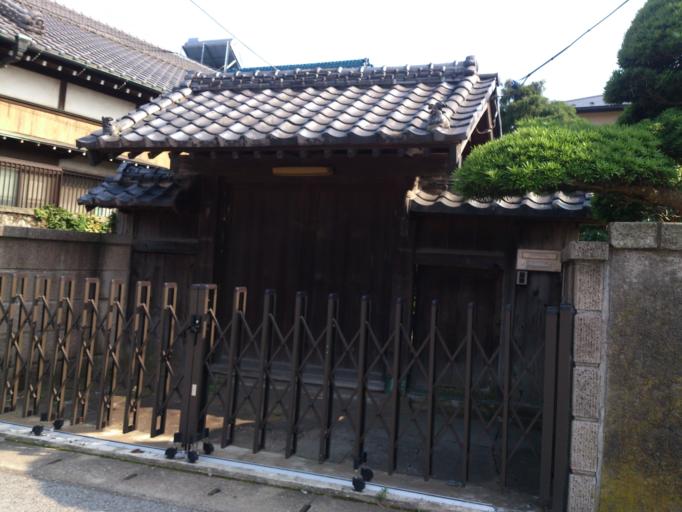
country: JP
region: Chiba
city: Funabashi
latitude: 35.6624
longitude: 140.0509
